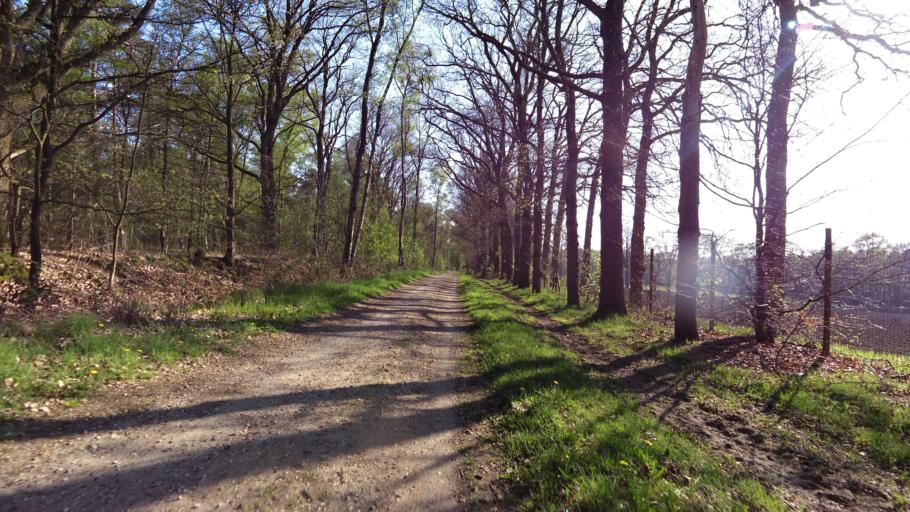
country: NL
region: Gelderland
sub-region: Gemeente Renkum
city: Oosterbeek
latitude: 52.0215
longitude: 5.8362
